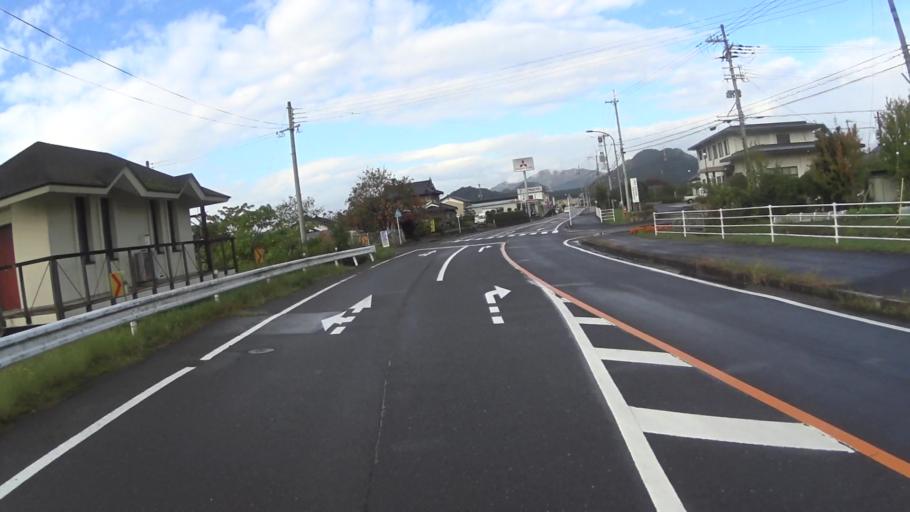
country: JP
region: Kyoto
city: Ayabe
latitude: 35.3088
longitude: 135.2262
